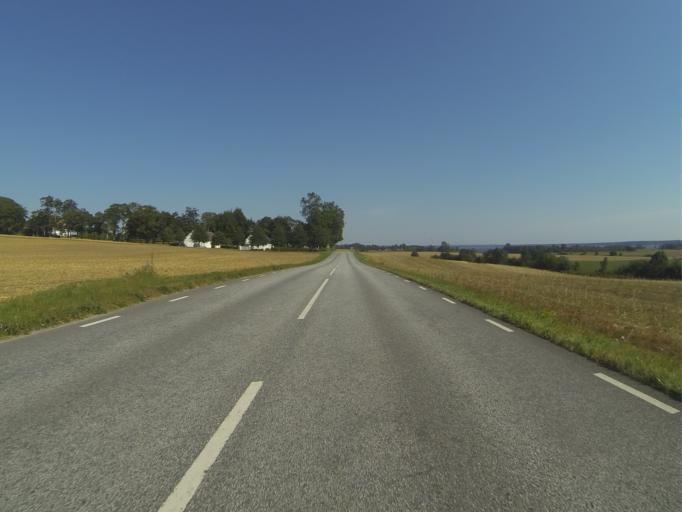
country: SE
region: Skane
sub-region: Hoors Kommun
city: Loberod
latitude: 55.7113
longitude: 13.5455
